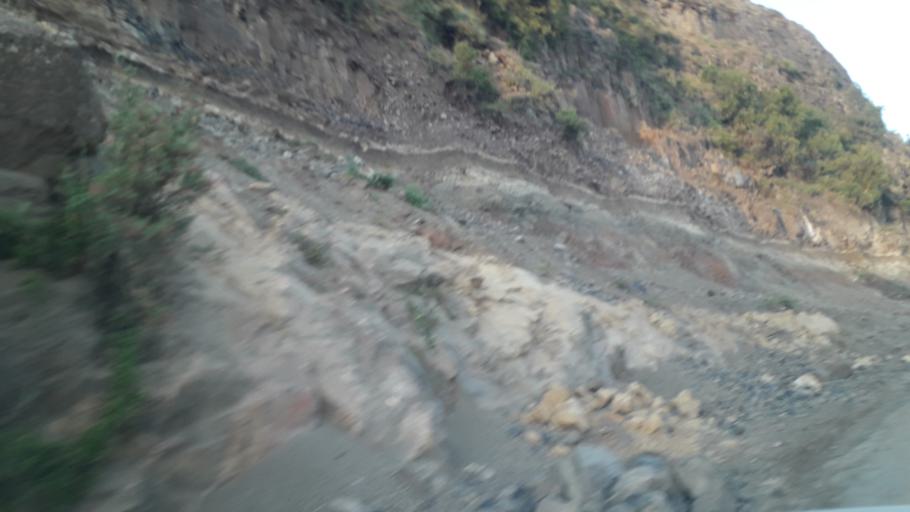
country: ET
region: Amhara
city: Lalibela
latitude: 11.5533
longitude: 39.2167
